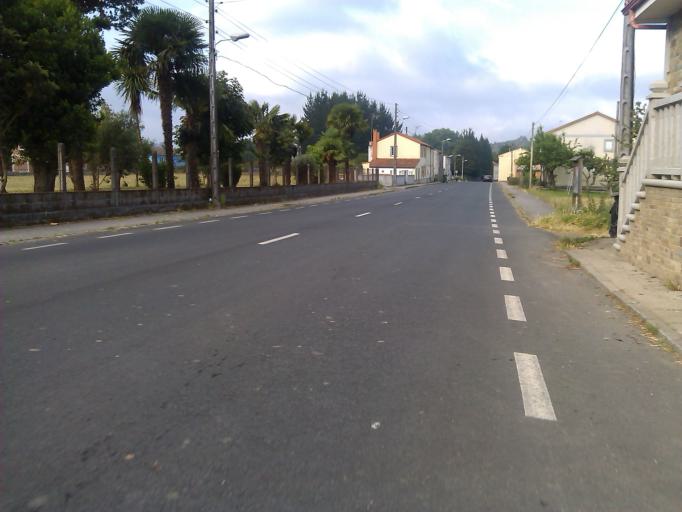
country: ES
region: Galicia
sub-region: Provincia da Coruna
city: Melide
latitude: 42.9105
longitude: -8.0254
